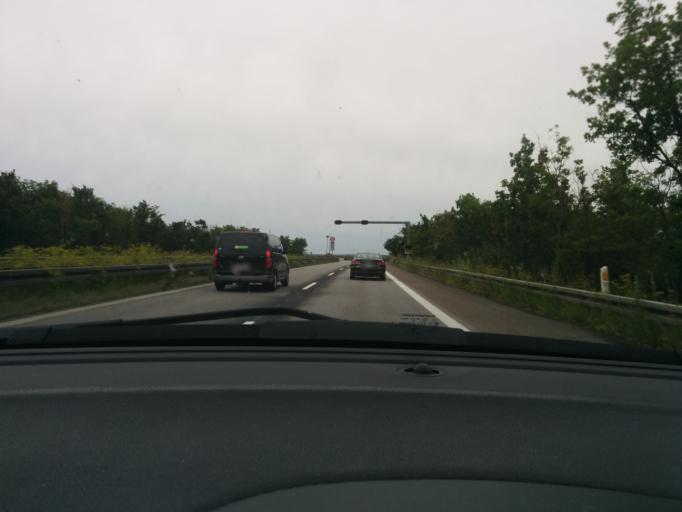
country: DK
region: Zealand
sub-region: Vordingborg Kommune
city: Nyrad
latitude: 54.9721
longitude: 12.0036
